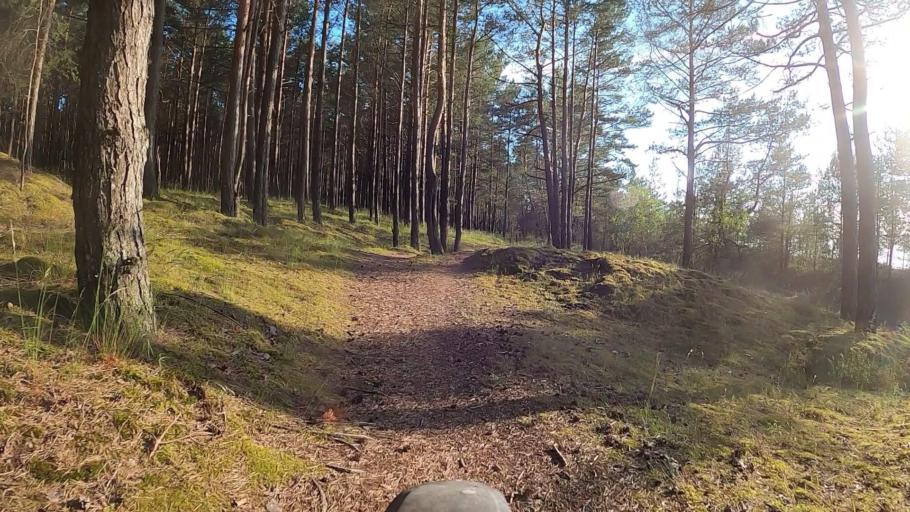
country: LV
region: Carnikava
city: Carnikava
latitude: 57.1216
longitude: 24.2069
